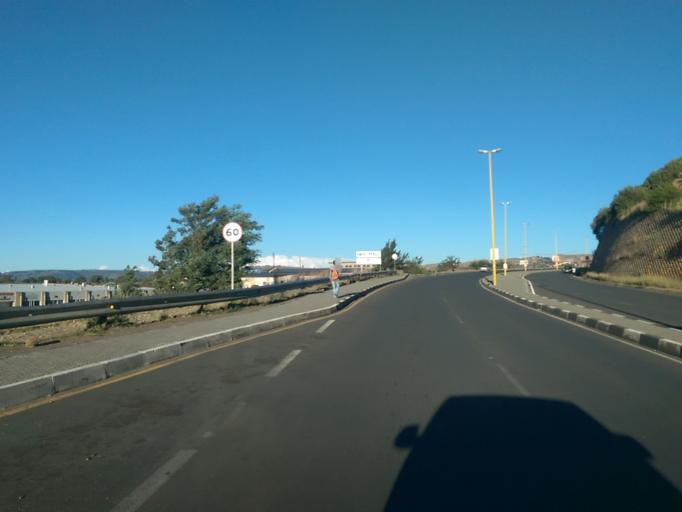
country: LS
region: Maseru
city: Maseru
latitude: -29.3168
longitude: 27.4888
